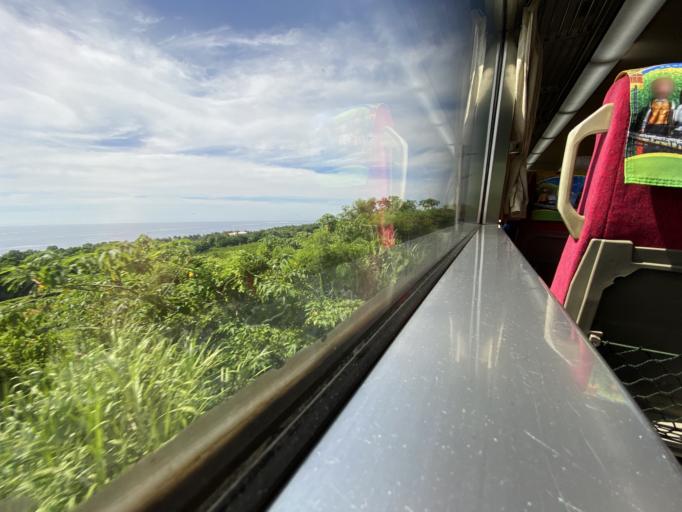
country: TW
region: Taiwan
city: Taitung City
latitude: 22.6233
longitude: 121.0079
